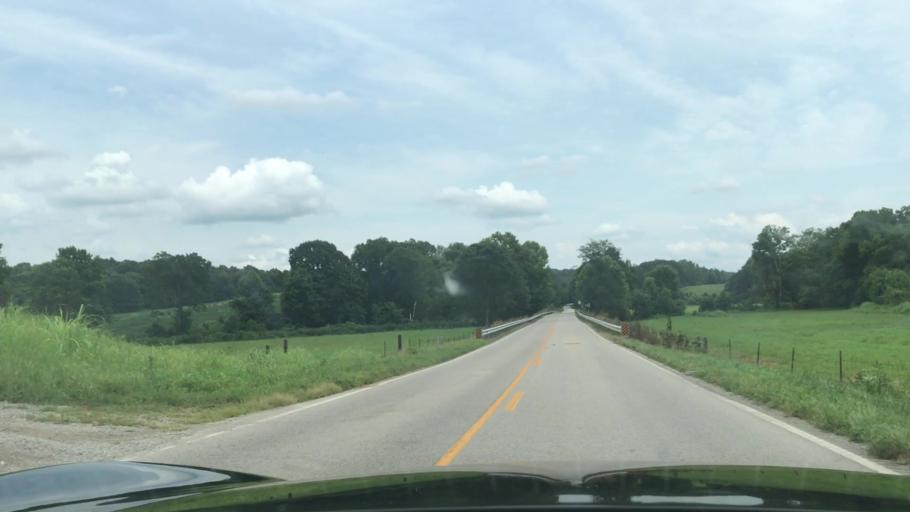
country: US
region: Kentucky
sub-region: Butler County
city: Morgantown
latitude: 37.1768
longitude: -86.8500
